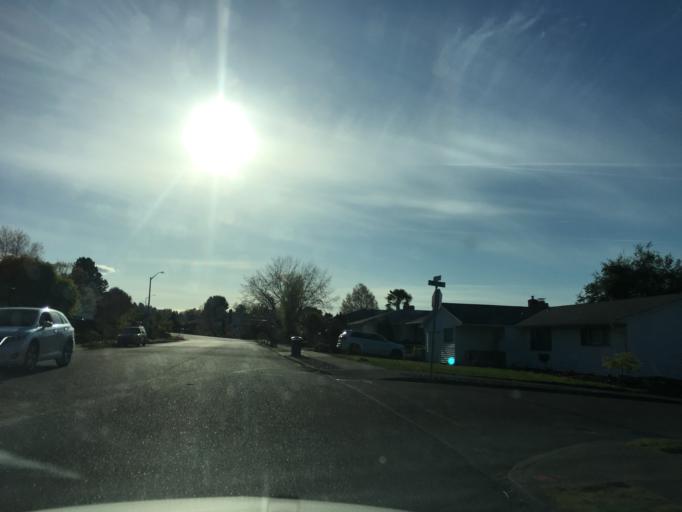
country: US
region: Oregon
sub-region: Multnomah County
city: Lents
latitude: 45.5522
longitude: -122.5277
